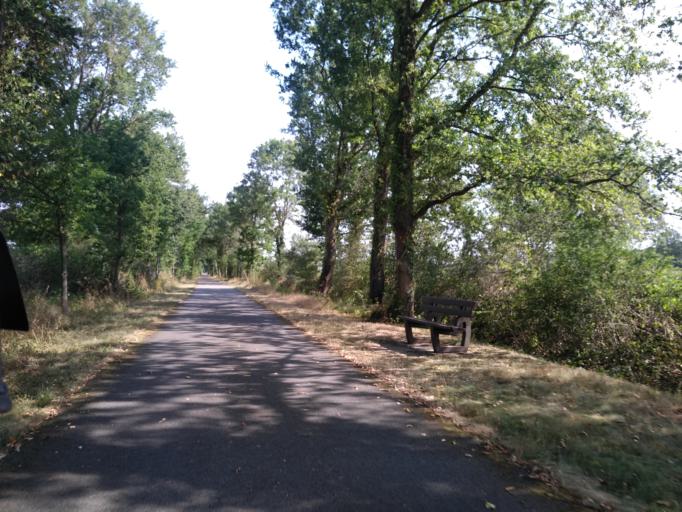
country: FR
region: Bourgogne
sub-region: Departement de Saone-et-Loire
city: Marcigny
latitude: 46.3171
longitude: 4.0285
